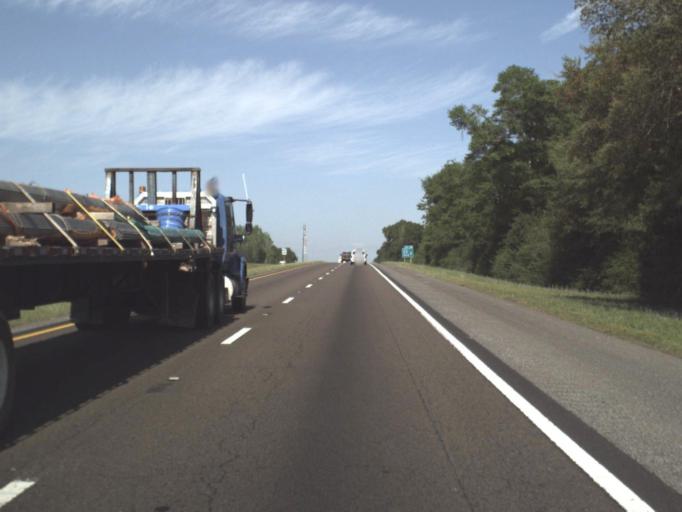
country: US
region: Florida
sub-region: Okaloosa County
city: Crestview
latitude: 30.6943
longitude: -86.7623
